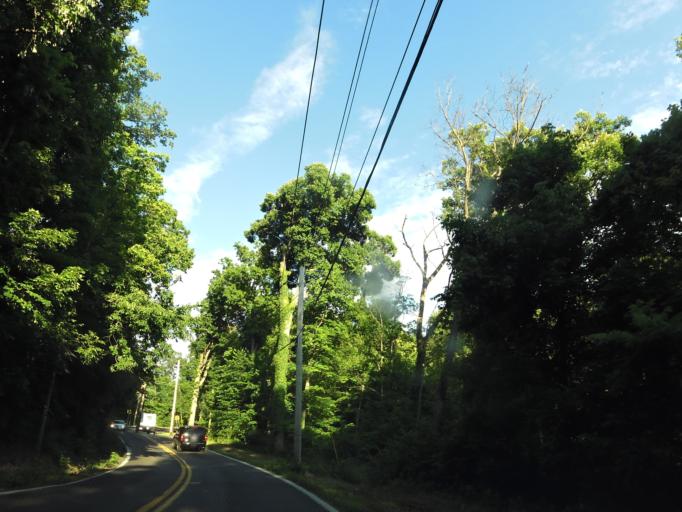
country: US
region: Missouri
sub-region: Saint Louis County
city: Wildwood
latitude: 38.6444
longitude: -90.6730
